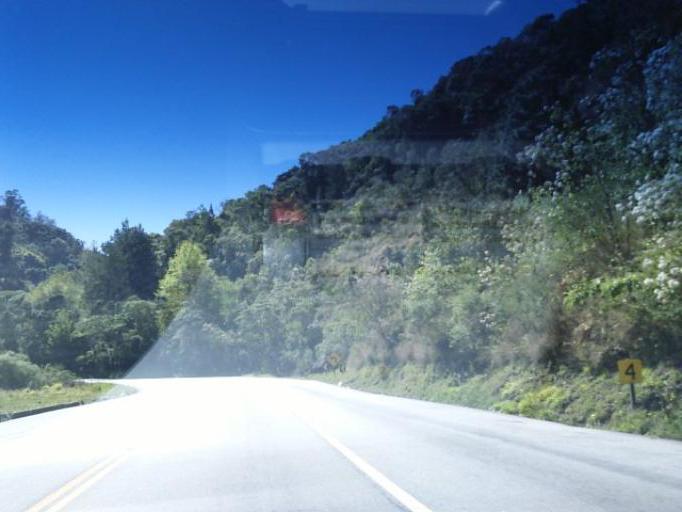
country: BR
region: Sao Paulo
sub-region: Campos Do Jordao
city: Campos do Jordao
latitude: -22.7783
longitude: -45.6102
